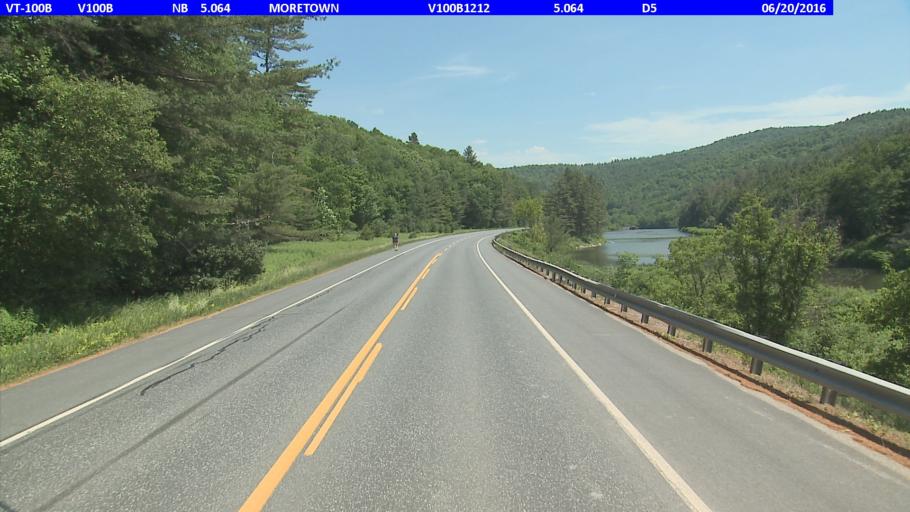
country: US
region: Vermont
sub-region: Washington County
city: Waterbury
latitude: 44.2899
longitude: -72.7179
